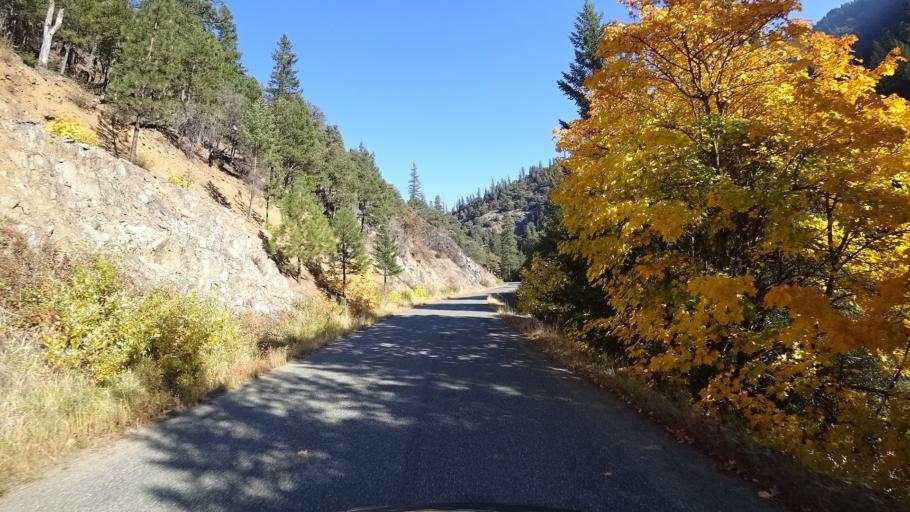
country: US
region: California
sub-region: Siskiyou County
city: Happy Camp
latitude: 41.6559
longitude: -123.1137
